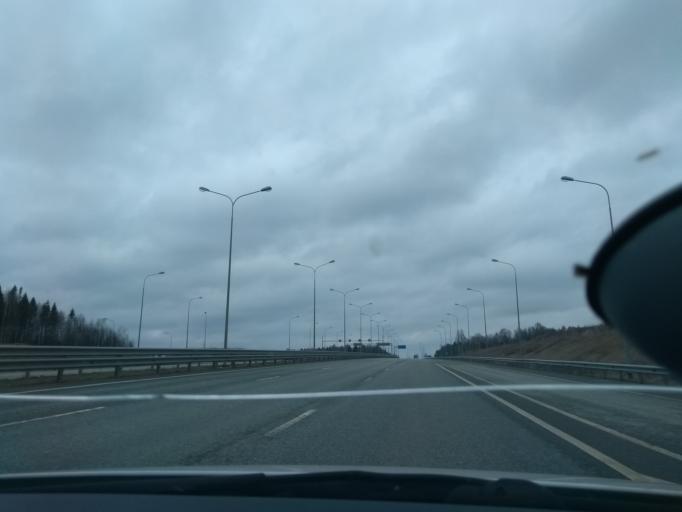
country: RU
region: Perm
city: Zvezdnyy
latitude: 57.7343
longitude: 56.3444
